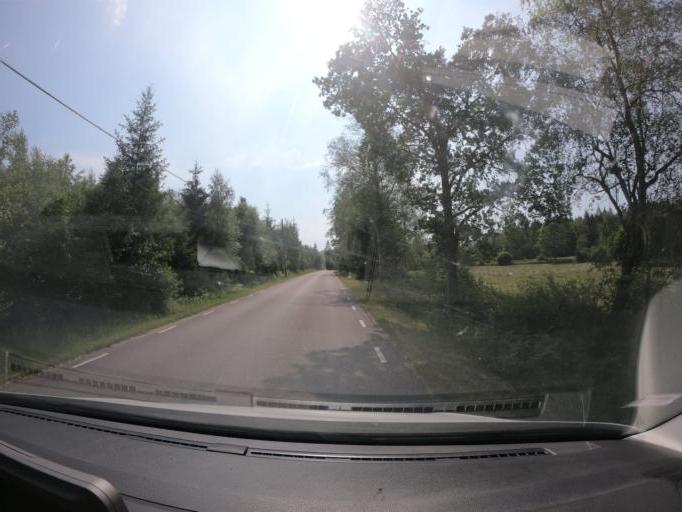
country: SE
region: Skane
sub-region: Hassleholms Kommun
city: Bjarnum
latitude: 56.3318
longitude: 13.6211
